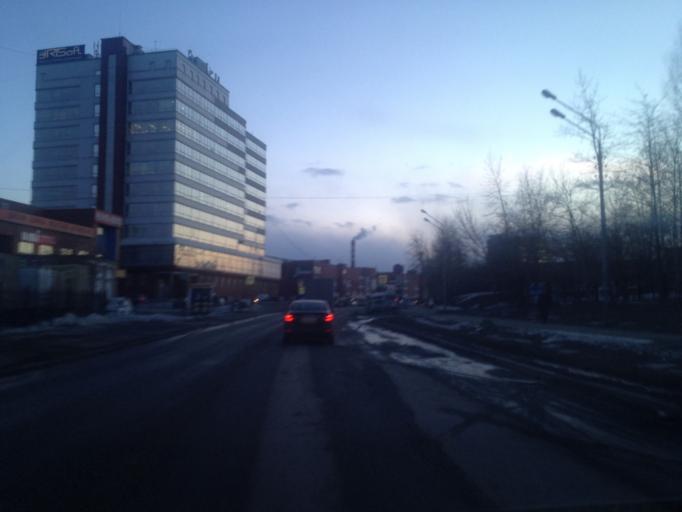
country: RU
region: Sverdlovsk
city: Yekaterinburg
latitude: 56.7887
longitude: 60.6322
